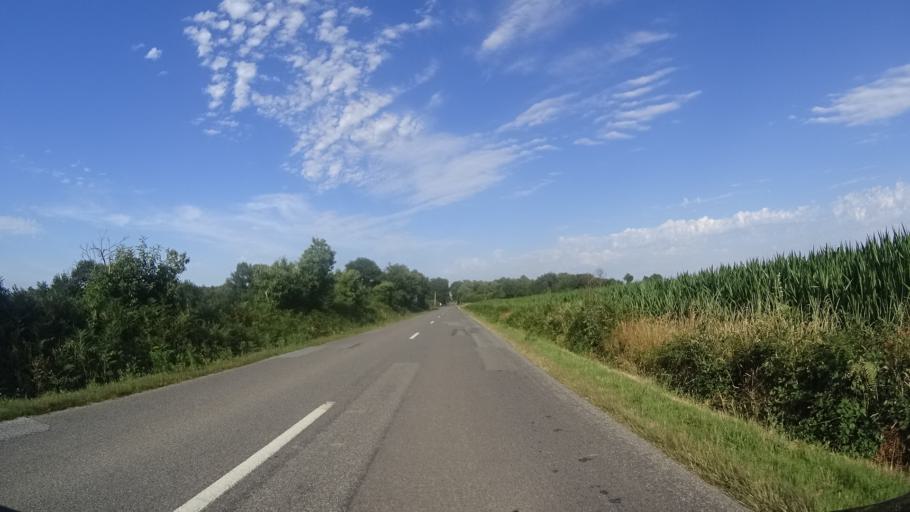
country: FR
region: Brittany
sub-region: Departement du Morbihan
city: Allaire
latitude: 47.6107
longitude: -2.1941
